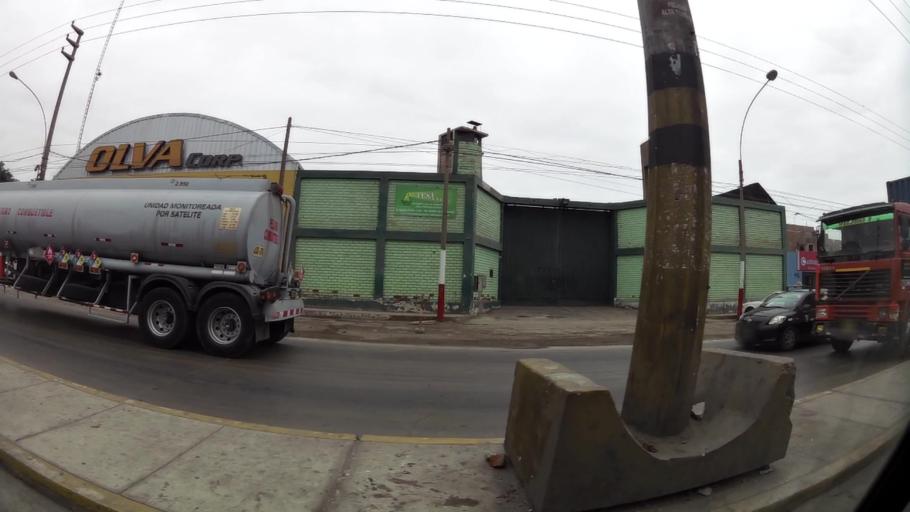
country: PE
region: Callao
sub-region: Callao
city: Callao
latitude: -12.0485
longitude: -77.0997
